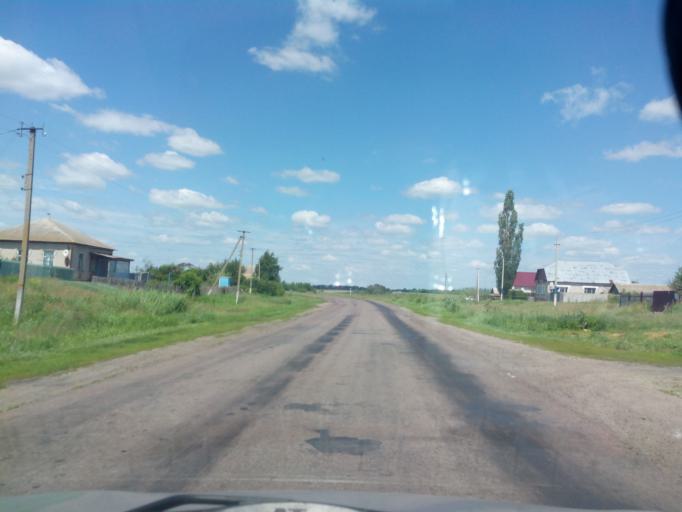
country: RU
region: Tambov
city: Zherdevka
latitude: 51.7603
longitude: 41.5113
